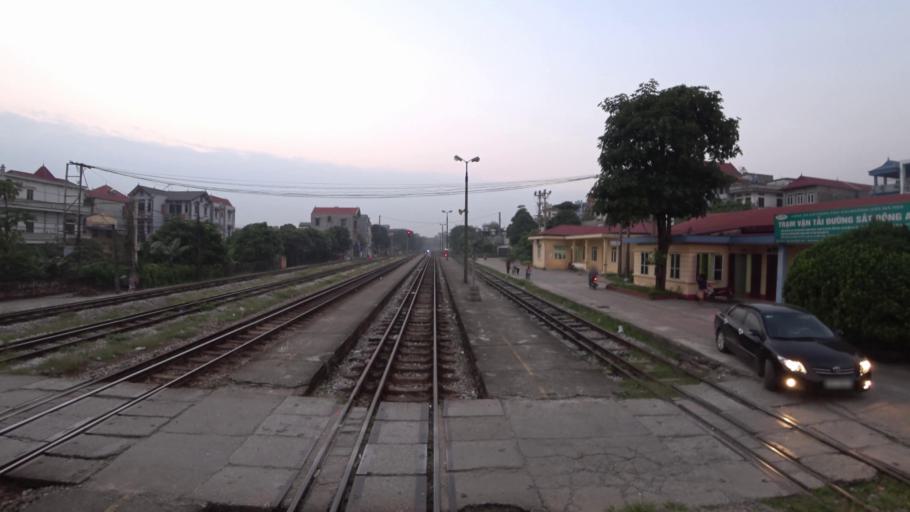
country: VN
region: Ha Noi
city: Soc Son
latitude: 21.2148
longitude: 105.8583
